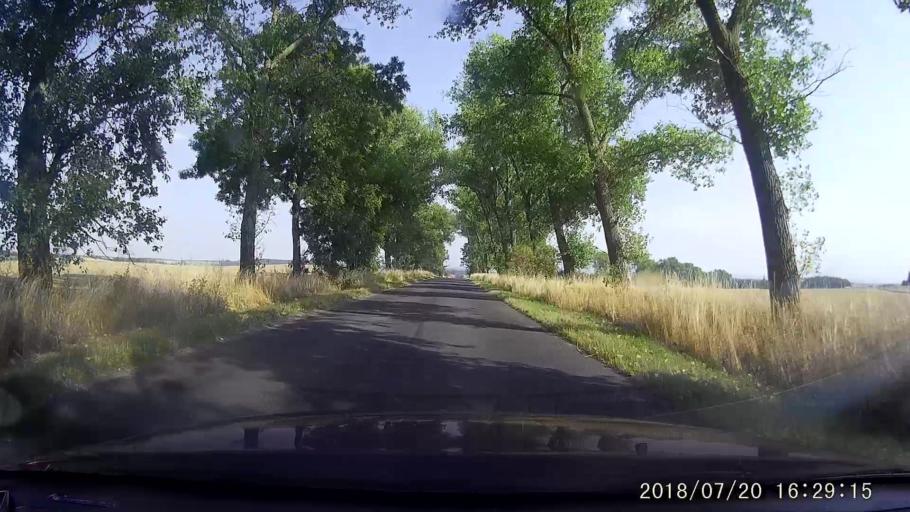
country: PL
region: Lower Silesian Voivodeship
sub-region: Powiat zgorzelecki
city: Sulikow
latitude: 51.1135
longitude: 15.0653
